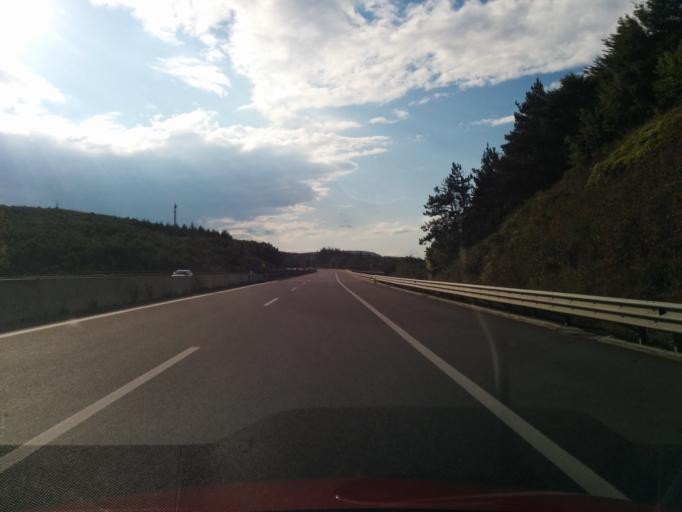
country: AT
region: Lower Austria
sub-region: Politischer Bezirk Wien-Umgebung
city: Wolfsgraben
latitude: 48.1745
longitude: 16.1257
